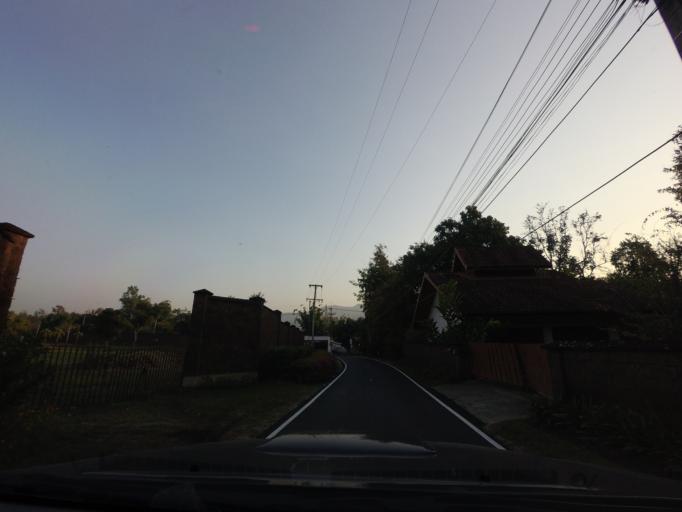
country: TH
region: Chiang Mai
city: Chiang Mai
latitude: 18.9238
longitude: 98.9092
